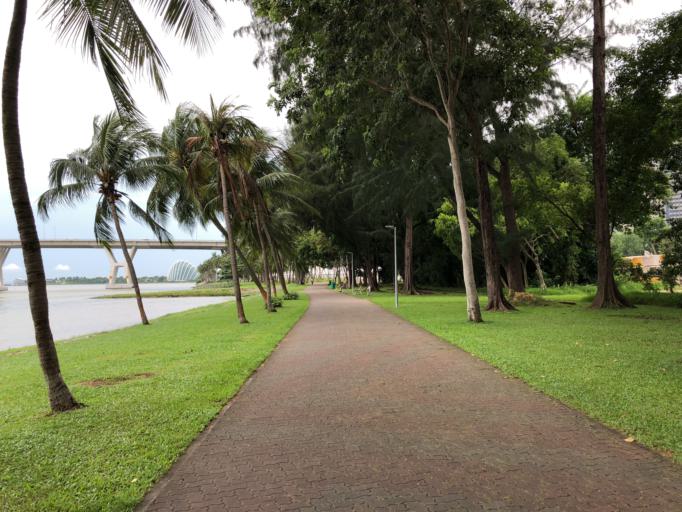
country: SG
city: Singapore
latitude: 1.2979
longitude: 103.8640
